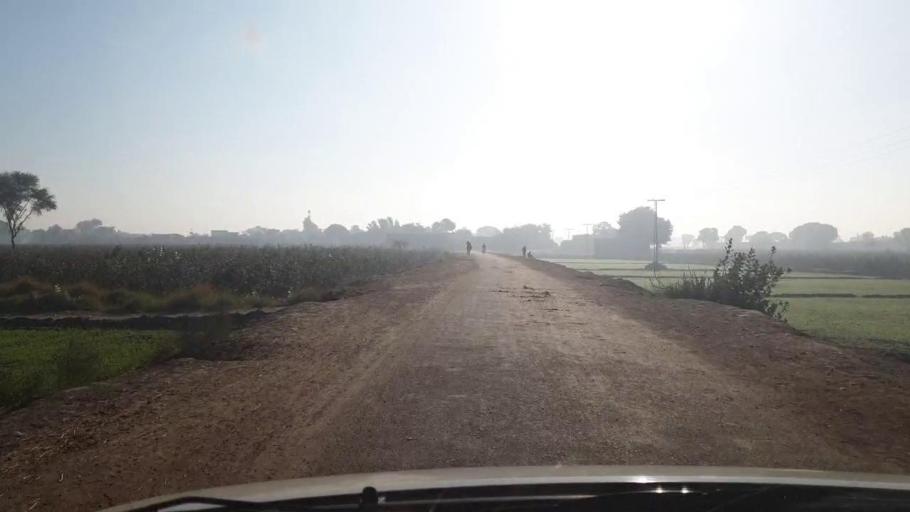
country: PK
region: Sindh
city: Dadu
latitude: 26.6837
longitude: 67.7784
